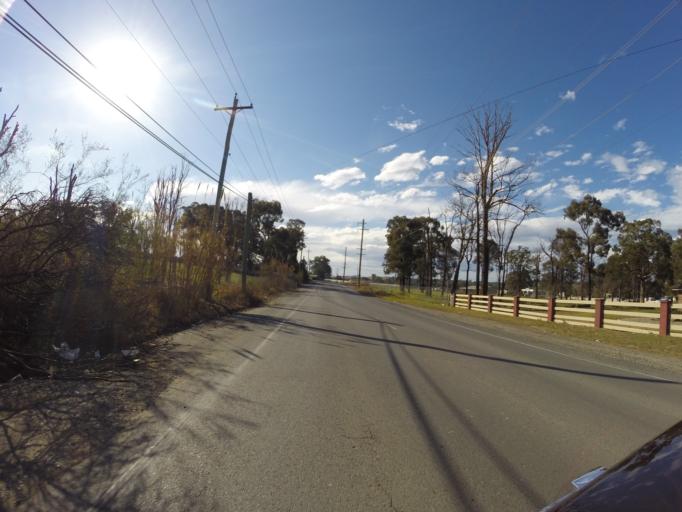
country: AU
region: New South Wales
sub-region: Fairfield
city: Cecil Park
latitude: -33.8817
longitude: 150.7925
